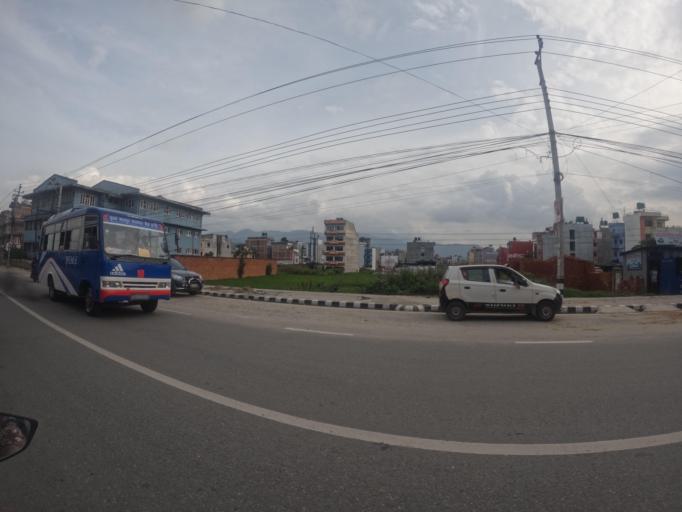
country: NP
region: Central Region
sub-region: Bagmati Zone
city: Bhaktapur
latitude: 27.6802
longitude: 85.3979
